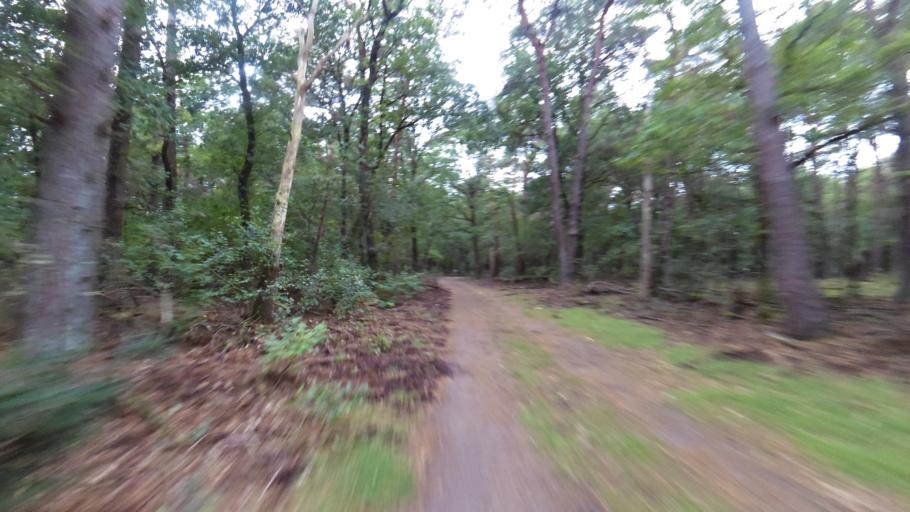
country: NL
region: Gelderland
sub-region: Gemeente Ede
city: Harskamp
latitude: 52.1829
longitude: 5.7869
